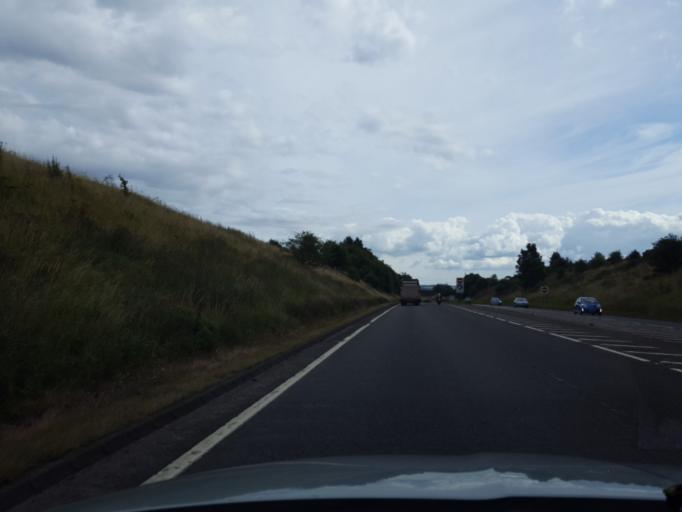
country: GB
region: Scotland
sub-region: Perth and Kinross
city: Luncarty
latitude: 56.4517
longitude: -3.4736
